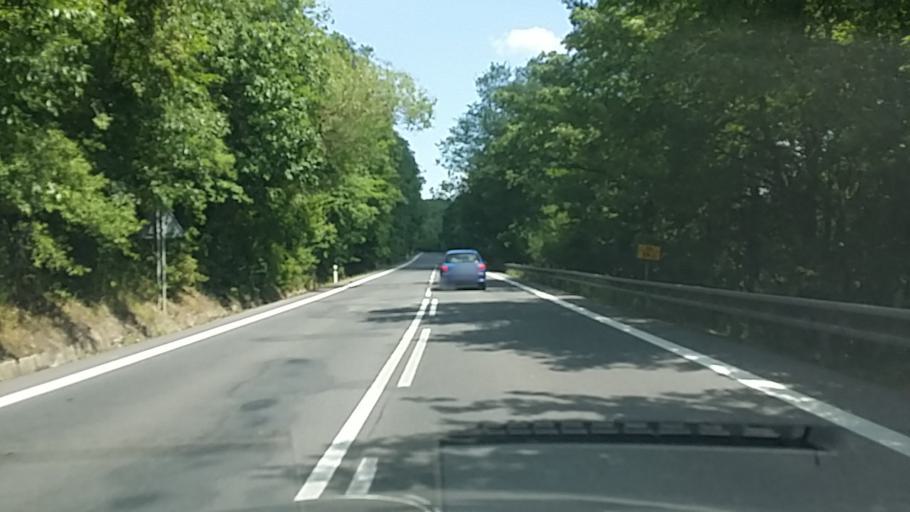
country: SK
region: Banskobystricky
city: Dudince
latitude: 48.2534
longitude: 18.9738
